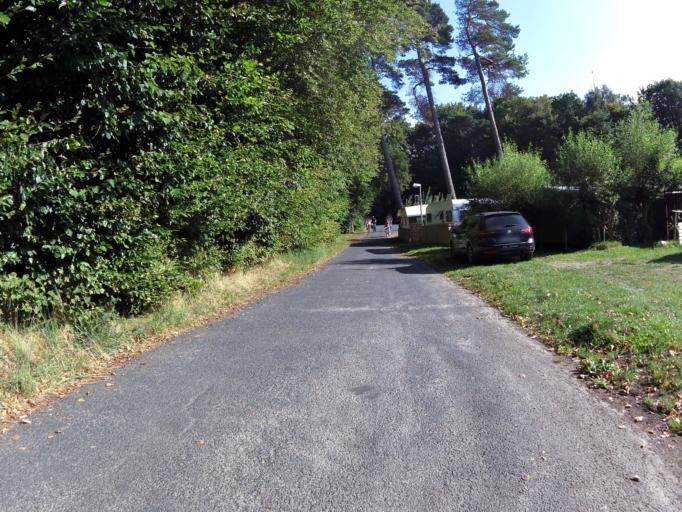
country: DE
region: Mecklenburg-Vorpommern
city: Seebad Bansin
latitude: 53.9943
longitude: 14.1095
